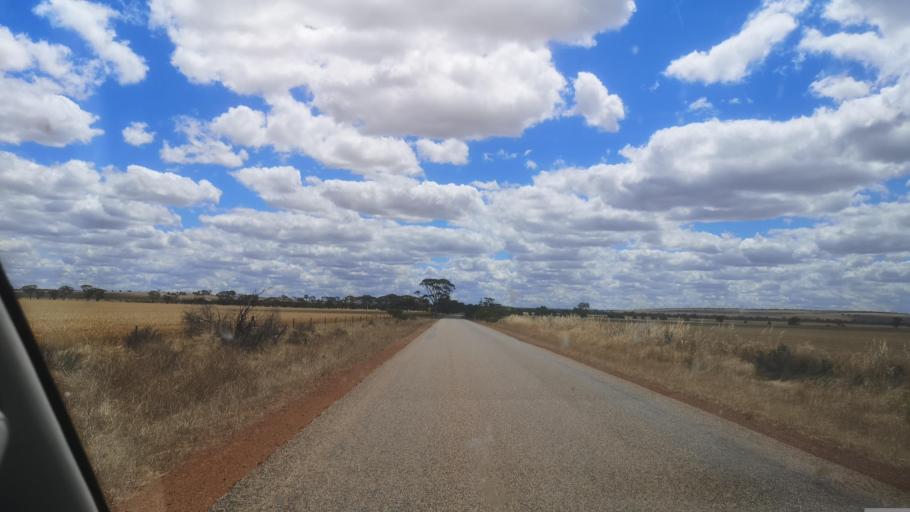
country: AU
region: Western Australia
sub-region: Cunderdin
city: Cunderdin
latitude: -32.0801
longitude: 117.4484
